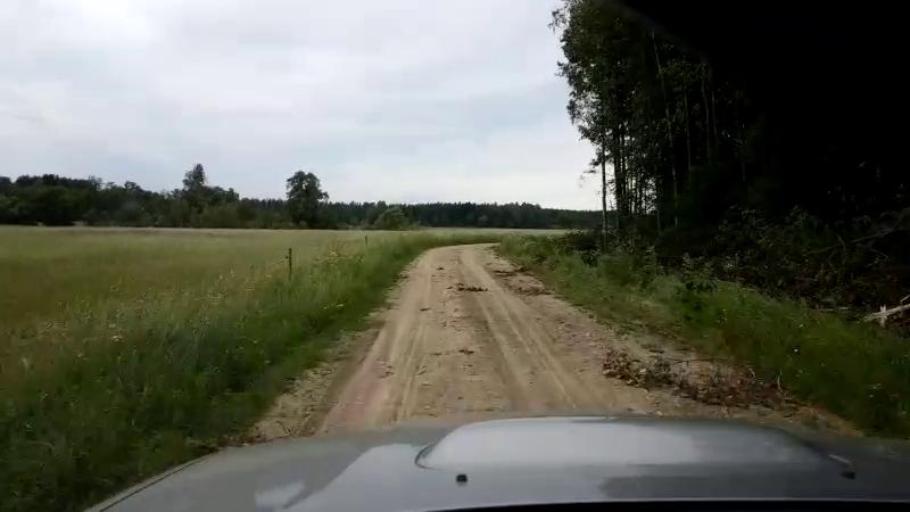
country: EE
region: Paernumaa
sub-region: Sindi linn
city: Sindi
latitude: 58.5119
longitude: 24.6201
